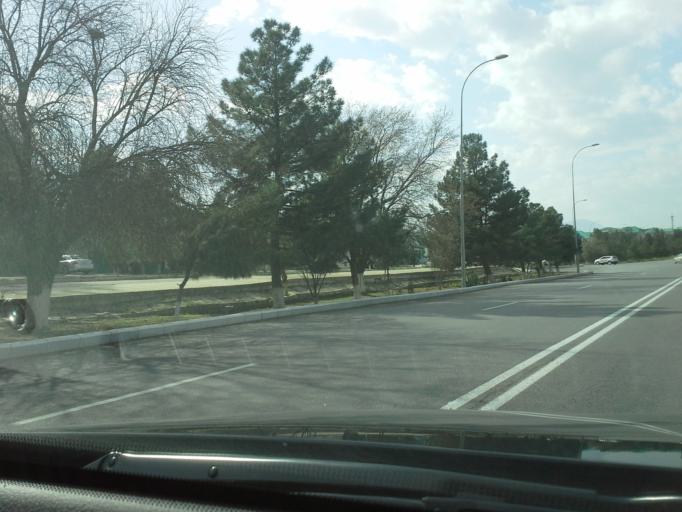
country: TM
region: Ahal
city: Ashgabat
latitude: 37.9580
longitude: 58.3215
